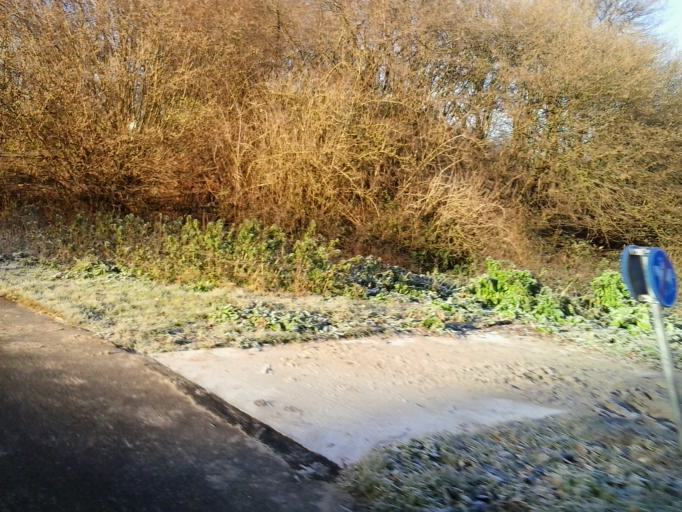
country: NL
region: South Holland
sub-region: Gemeente Lansingerland
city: Bergschenhoek
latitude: 51.9702
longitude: 4.5302
